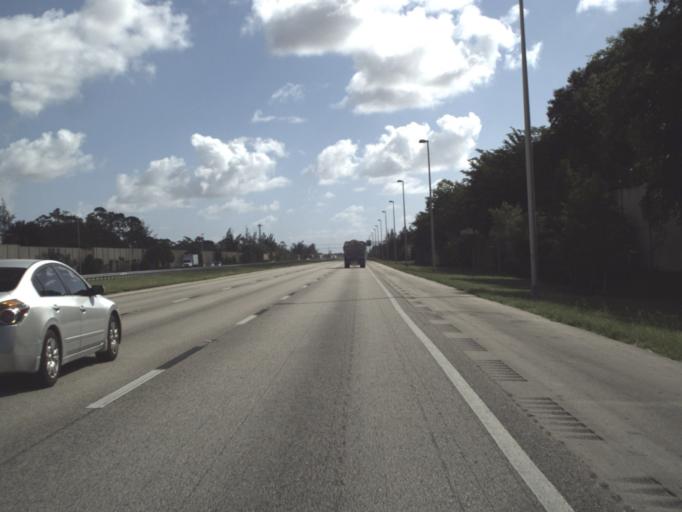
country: US
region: Florida
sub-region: Broward County
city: Parkland
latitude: 26.3006
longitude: -80.2287
